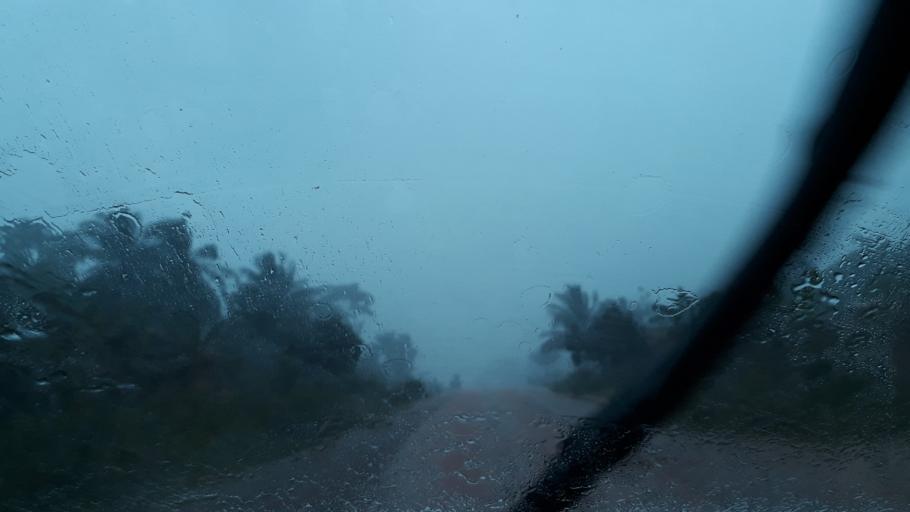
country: CD
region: Eastern Province
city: Kisangani
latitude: 0.4797
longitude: 25.6516
